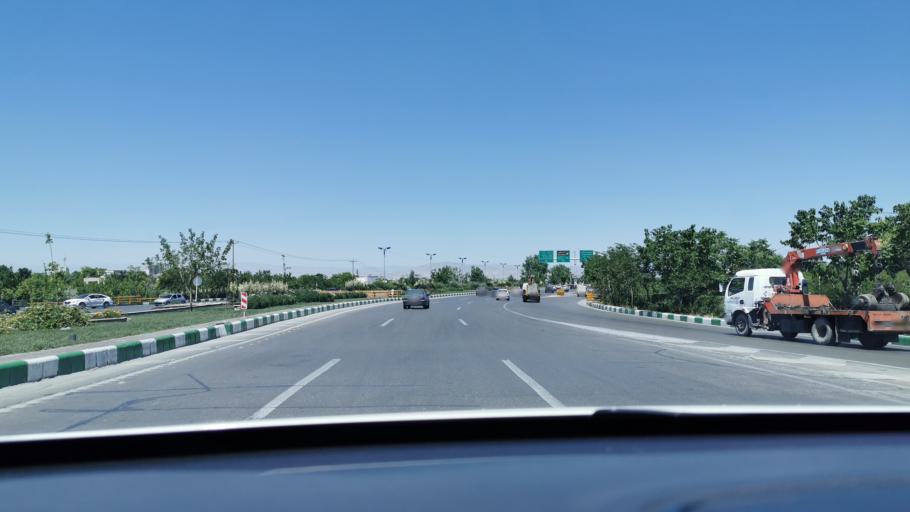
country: IR
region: Razavi Khorasan
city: Mashhad
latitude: 36.2504
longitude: 59.6116
